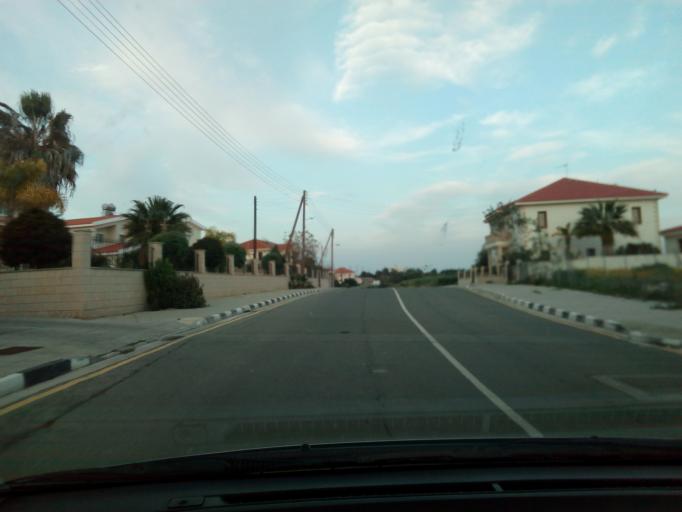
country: CY
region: Larnaka
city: Tersefanou
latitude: 34.8029
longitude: 33.4959
